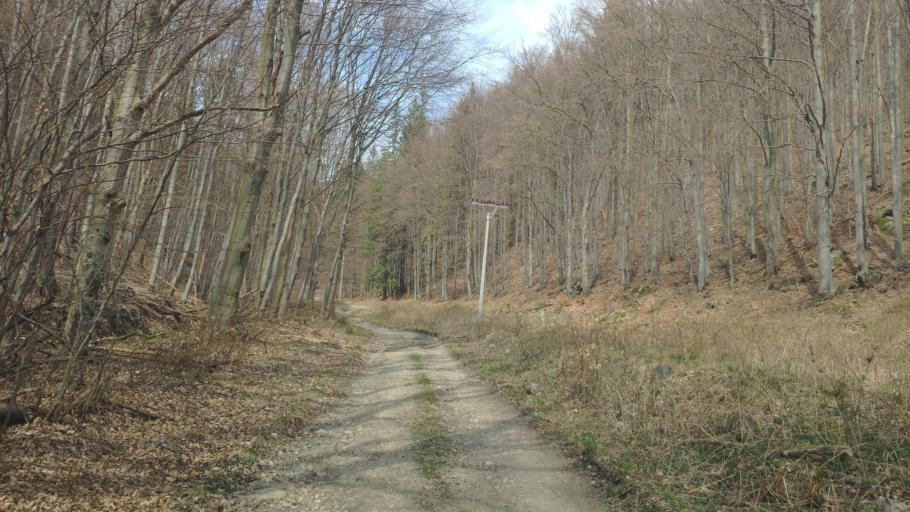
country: SK
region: Kosicky
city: Gelnica
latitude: 48.7518
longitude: 21.0272
